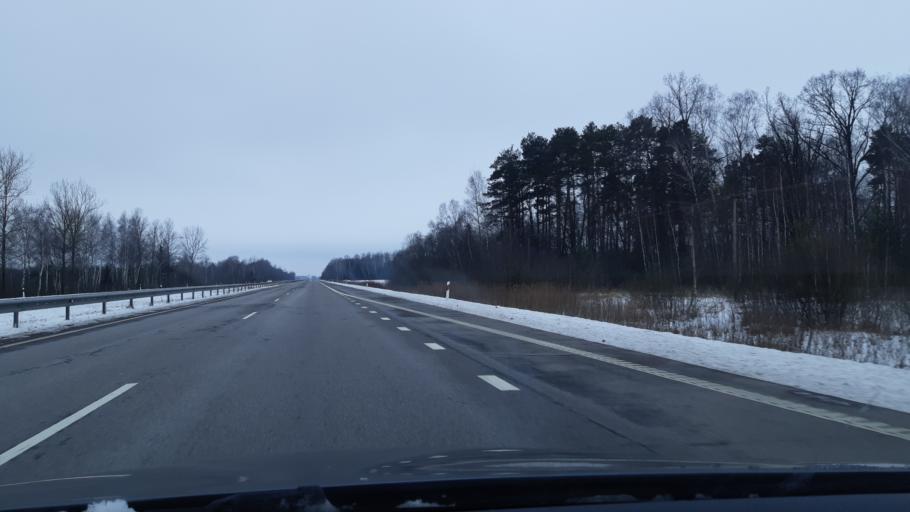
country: LT
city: Vilkija
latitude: 55.1260
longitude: 23.7471
